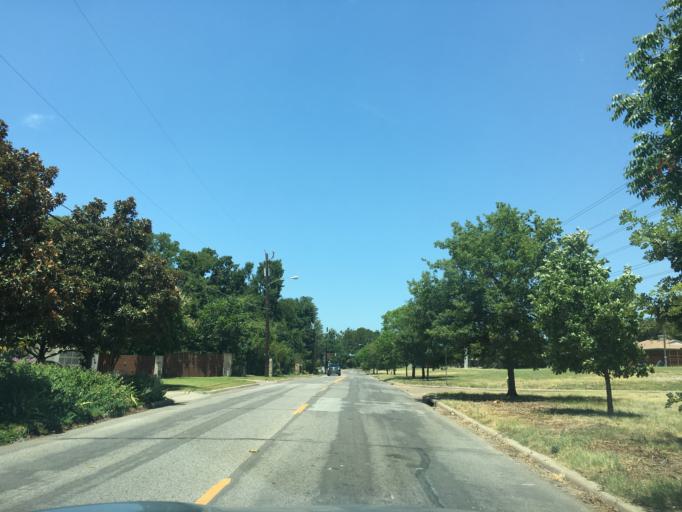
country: US
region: Texas
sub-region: Dallas County
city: Highland Park
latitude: 32.8376
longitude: -96.7433
